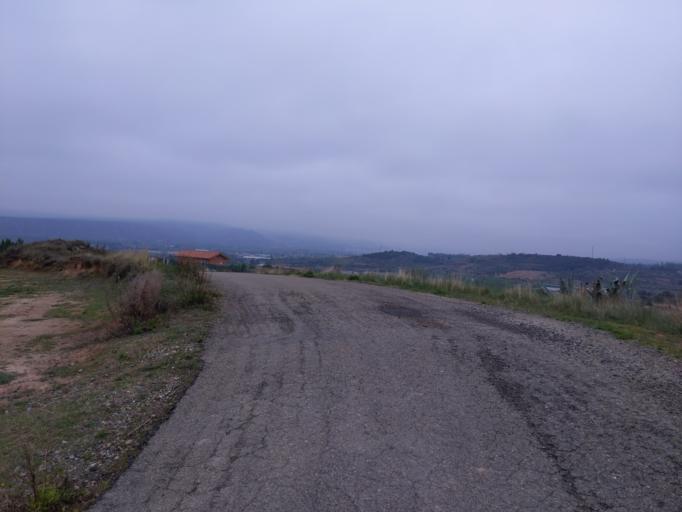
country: ES
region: La Rioja
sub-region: Provincia de La Rioja
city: Lardero
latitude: 42.4086
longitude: -2.4876
